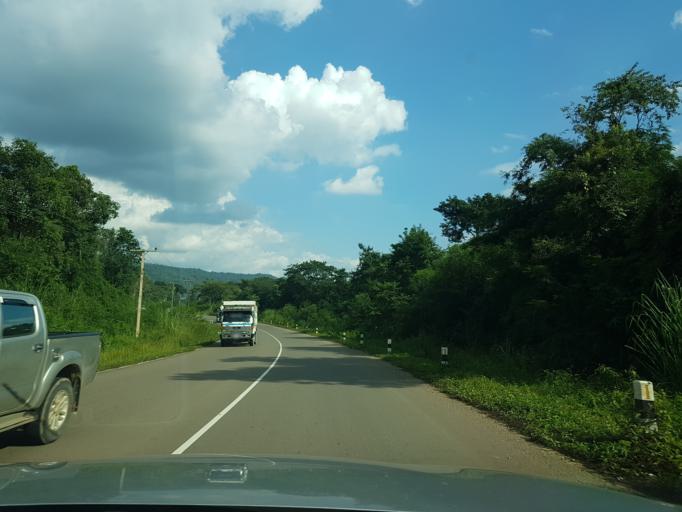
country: TH
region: Nong Khai
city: Sangkhom
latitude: 18.0322
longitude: 102.3693
